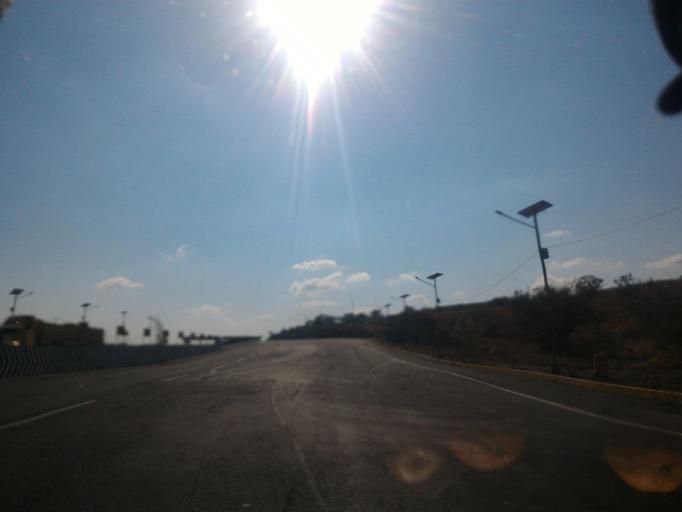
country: MX
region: Jalisco
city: Tonila
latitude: 19.4120
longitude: -103.5245
